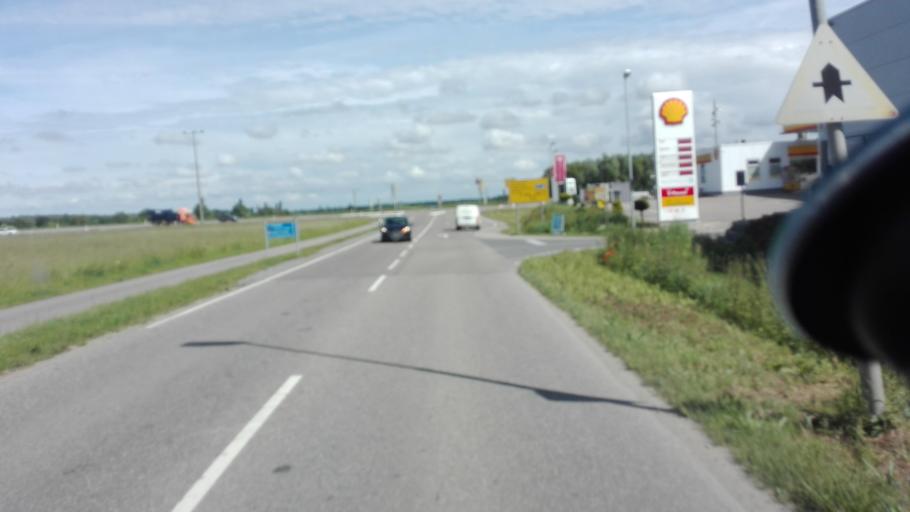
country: DE
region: Baden-Wuerttemberg
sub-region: Karlsruhe Region
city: Karlsdorf-Neuthard
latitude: 49.1489
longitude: 8.5456
